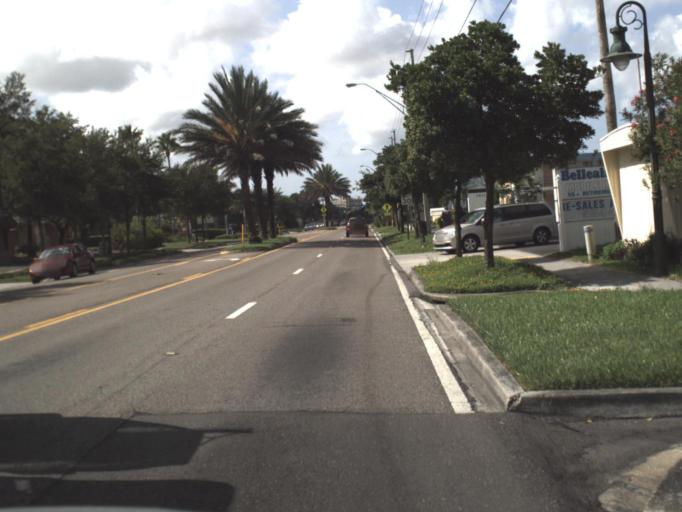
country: US
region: Florida
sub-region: Pinellas County
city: Belleair
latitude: 27.9269
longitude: -82.7962
